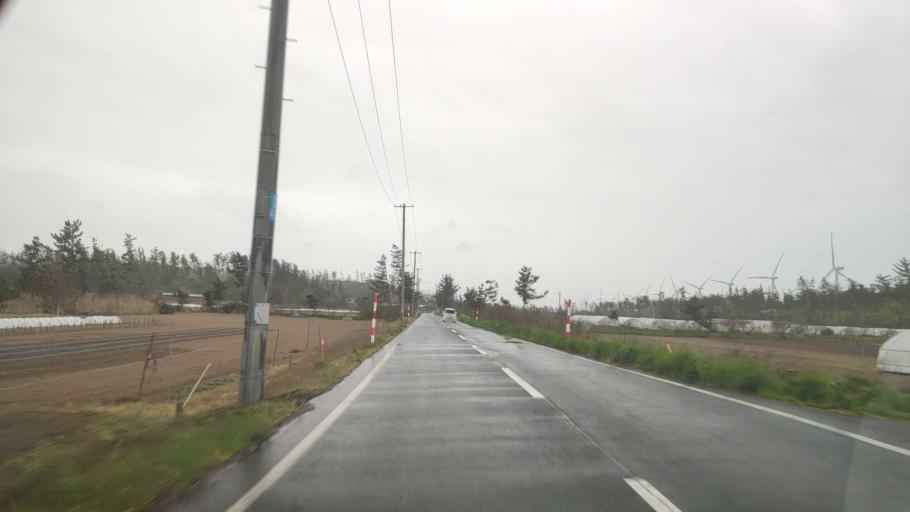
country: JP
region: Akita
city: Noshiromachi
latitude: 40.0937
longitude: 139.9622
